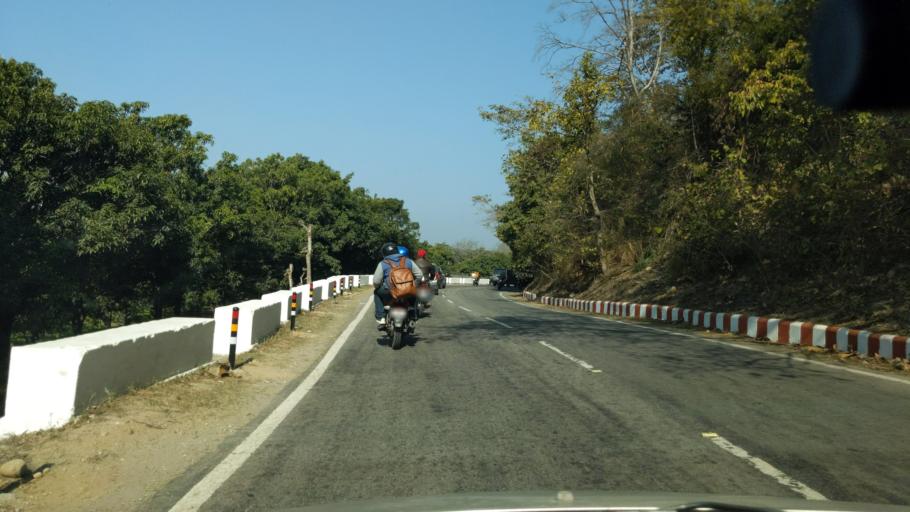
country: IN
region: Uttarakhand
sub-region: Naini Tal
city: Ramnagar
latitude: 29.3875
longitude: 79.1407
